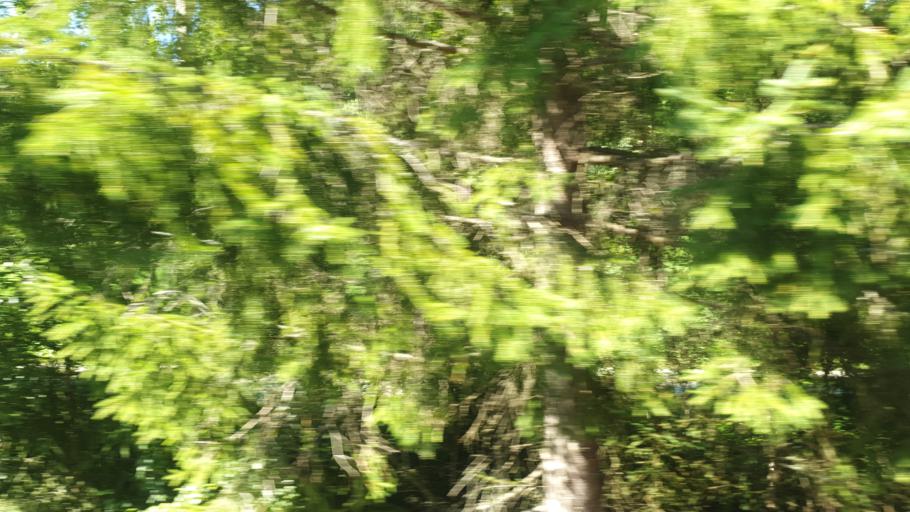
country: NO
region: Sor-Trondelag
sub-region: Meldal
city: Meldal
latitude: 63.1325
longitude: 9.7092
